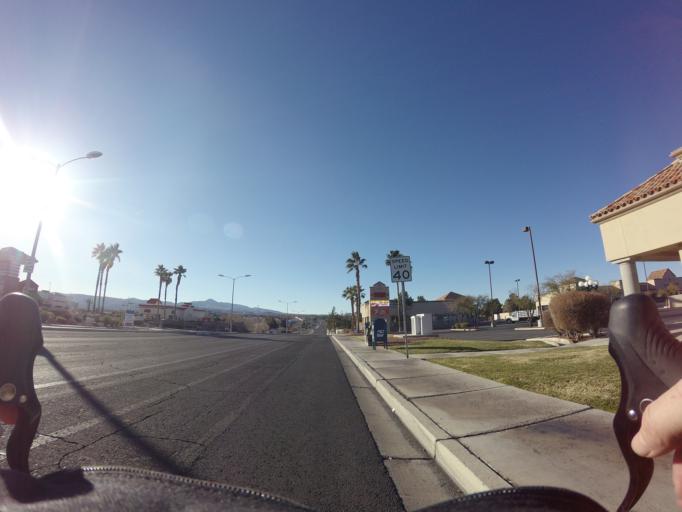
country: US
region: Nevada
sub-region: Clark County
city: Whitney
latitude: 36.0415
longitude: -115.1004
